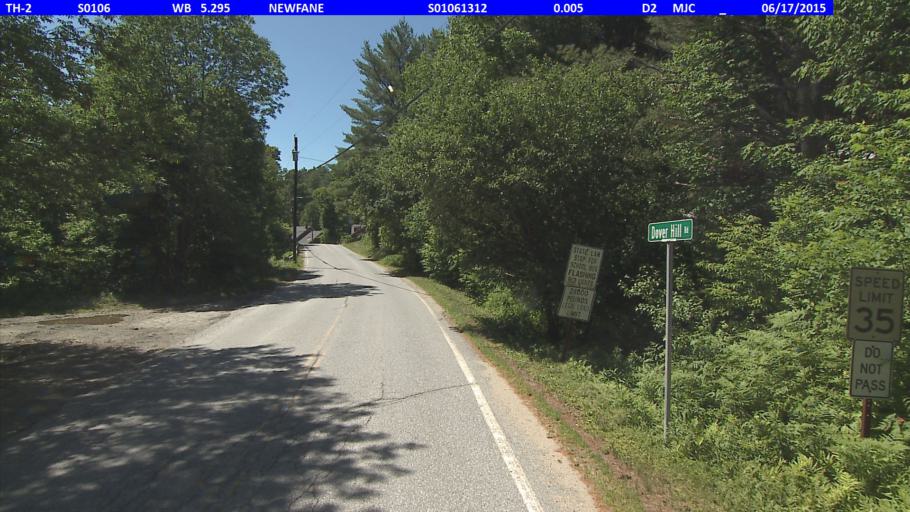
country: US
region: Vermont
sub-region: Windham County
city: Dover
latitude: 42.9507
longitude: -72.7658
